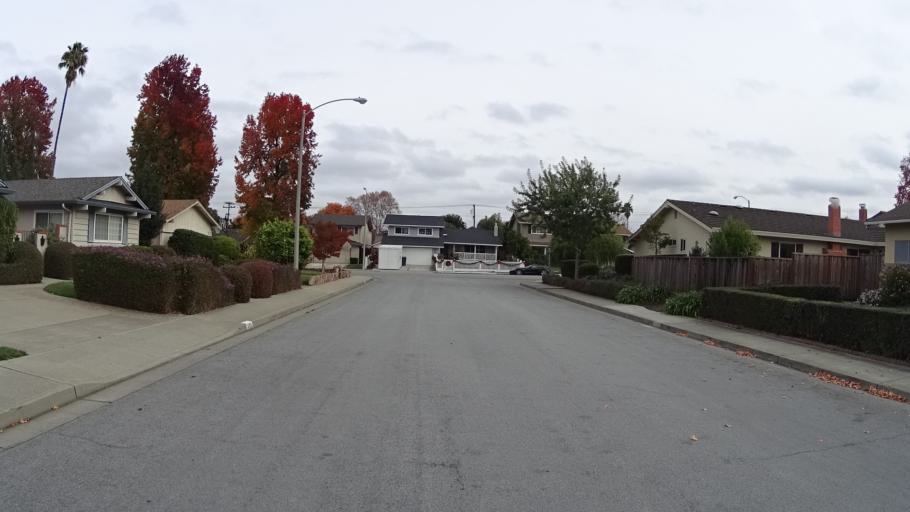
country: US
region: California
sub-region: Santa Clara County
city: Sunnyvale
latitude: 37.3616
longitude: -122.0489
